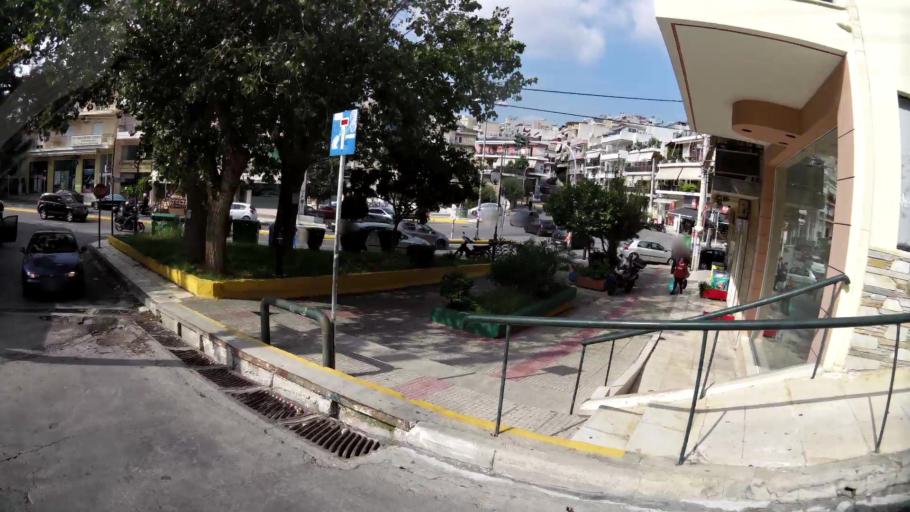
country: GR
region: Attica
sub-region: Nomarchia Athinas
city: Ymittos
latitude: 37.9460
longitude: 23.7593
